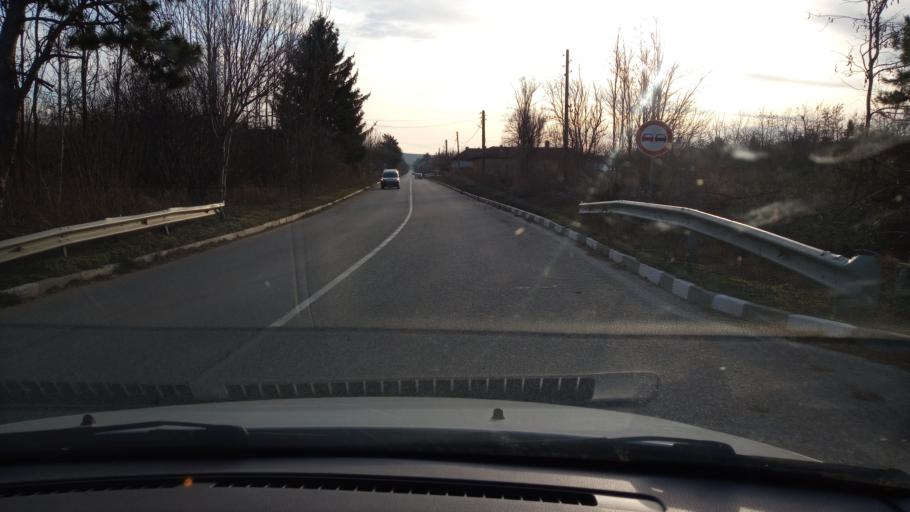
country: BG
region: Pleven
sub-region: Obshtina Pleven
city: Slavyanovo
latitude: 43.5619
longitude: 24.8696
